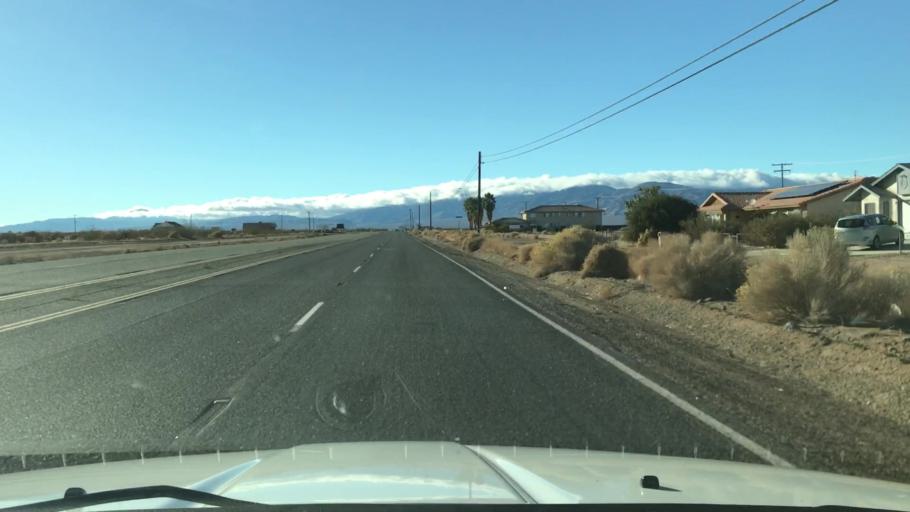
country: US
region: California
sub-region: Kern County
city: California City
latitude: 35.1258
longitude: -118.0079
